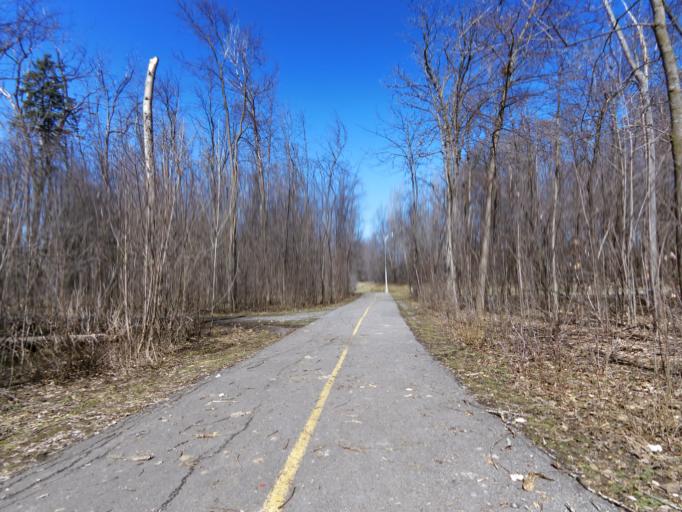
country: CA
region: Ontario
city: Ottawa
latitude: 45.4465
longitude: -75.6435
